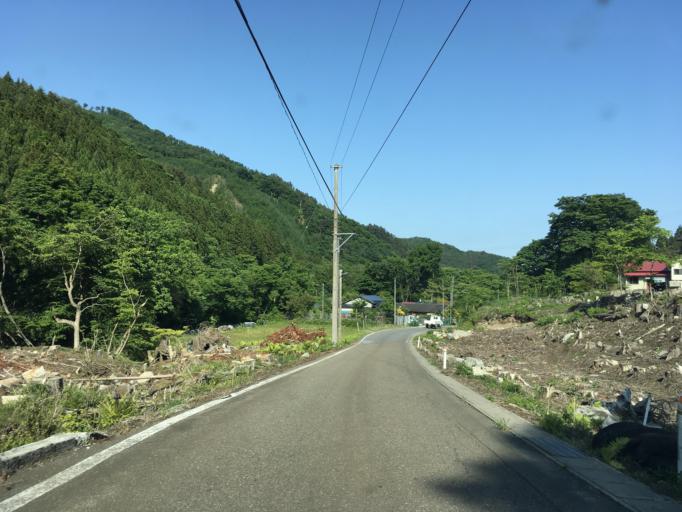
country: JP
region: Iwate
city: Kamaishi
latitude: 39.1978
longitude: 141.8286
